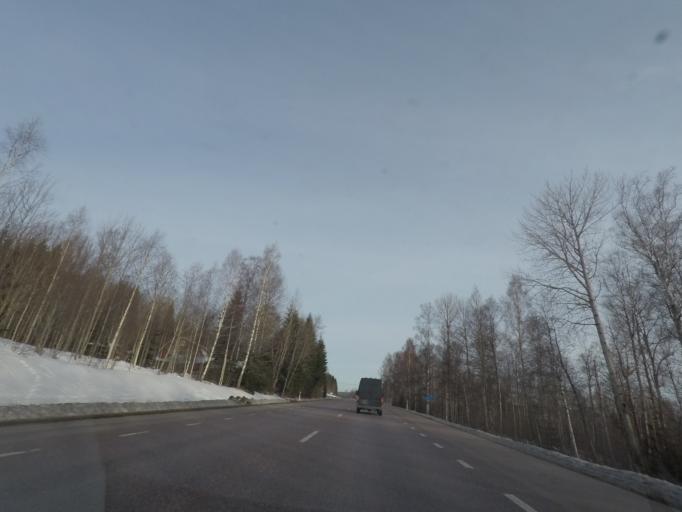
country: SE
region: Dalarna
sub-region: Smedjebackens Kommun
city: Smedjebacken
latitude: 60.1187
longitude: 15.4762
